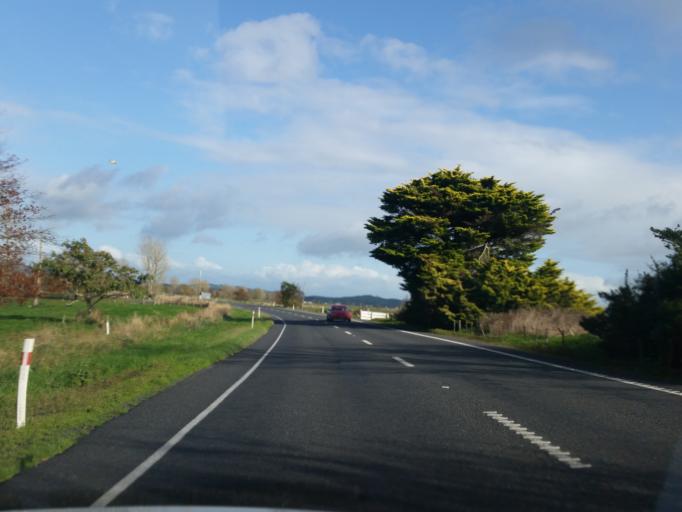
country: NZ
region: Waikato
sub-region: Hauraki District
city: Ngatea
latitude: -37.2761
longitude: 175.4652
